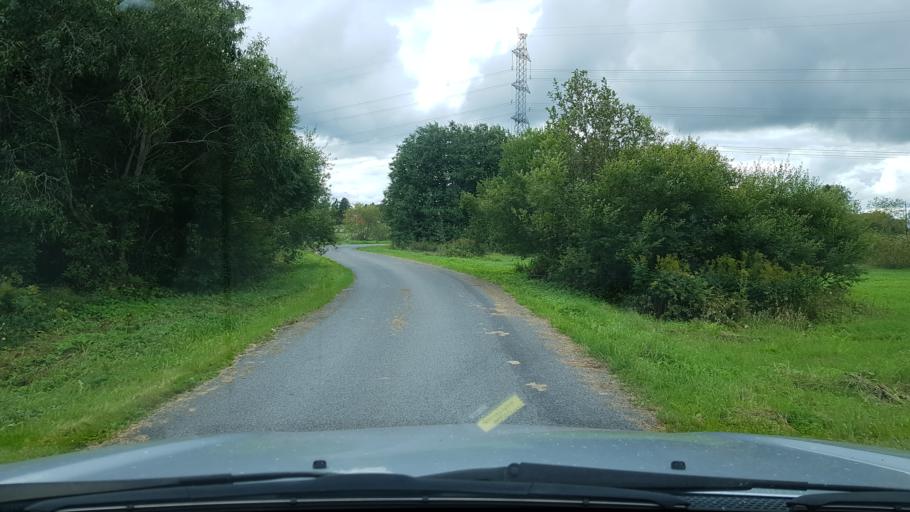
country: EE
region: Harju
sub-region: Rae vald
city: Vaida
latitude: 59.2959
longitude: 24.9930
